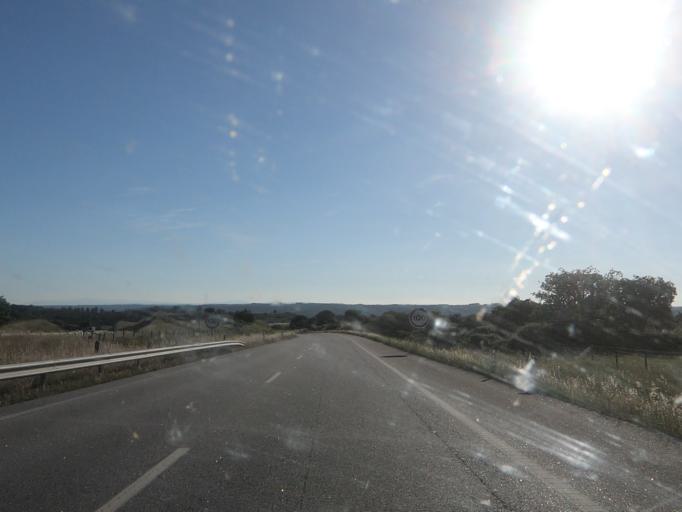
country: ES
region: Castille and Leon
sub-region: Provincia de Salamanca
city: Fuentes de Onoro
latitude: 40.6152
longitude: -6.8816
